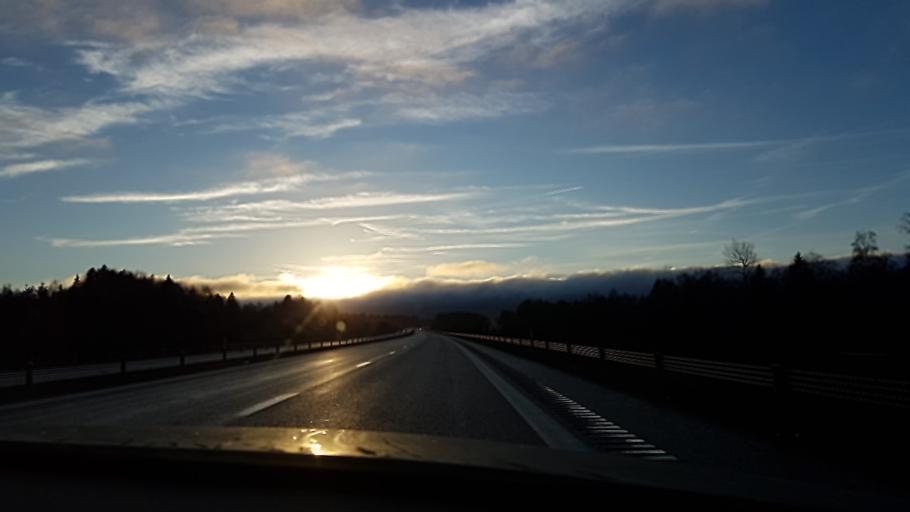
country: SE
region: Kronoberg
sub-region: Markaryds Kommun
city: Markaryd
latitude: 56.4416
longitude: 13.5878
